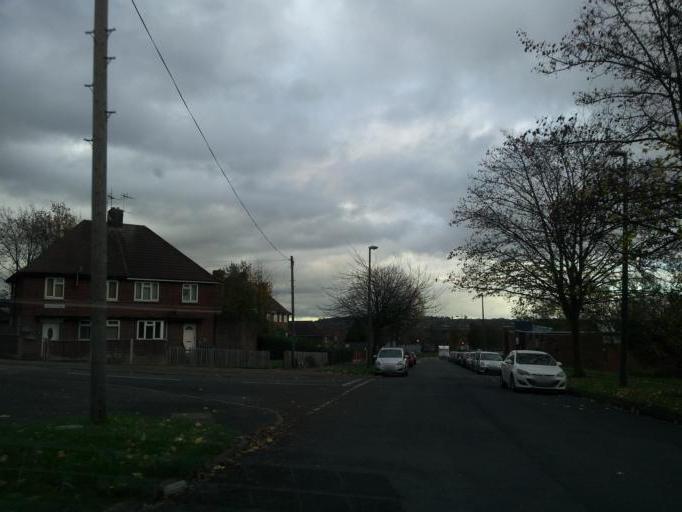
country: GB
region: England
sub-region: Nottinghamshire
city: Eastwood
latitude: 52.9919
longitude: -1.3118
